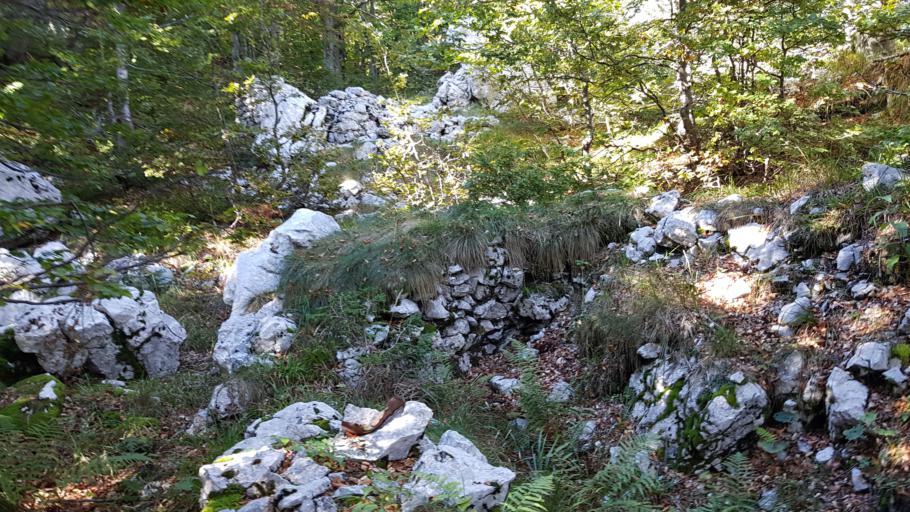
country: SI
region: Kobarid
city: Kobarid
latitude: 46.2910
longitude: 13.6088
